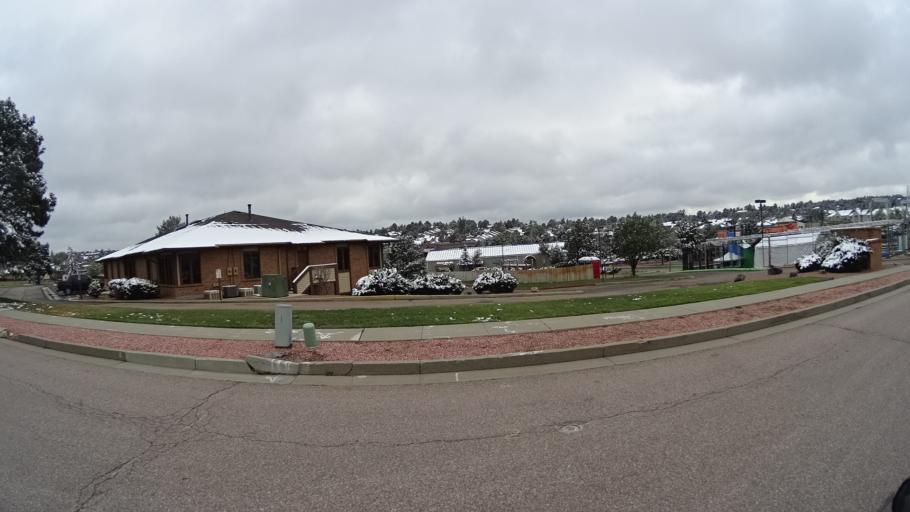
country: US
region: Colorado
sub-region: El Paso County
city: Colorado Springs
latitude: 38.9239
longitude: -104.7916
